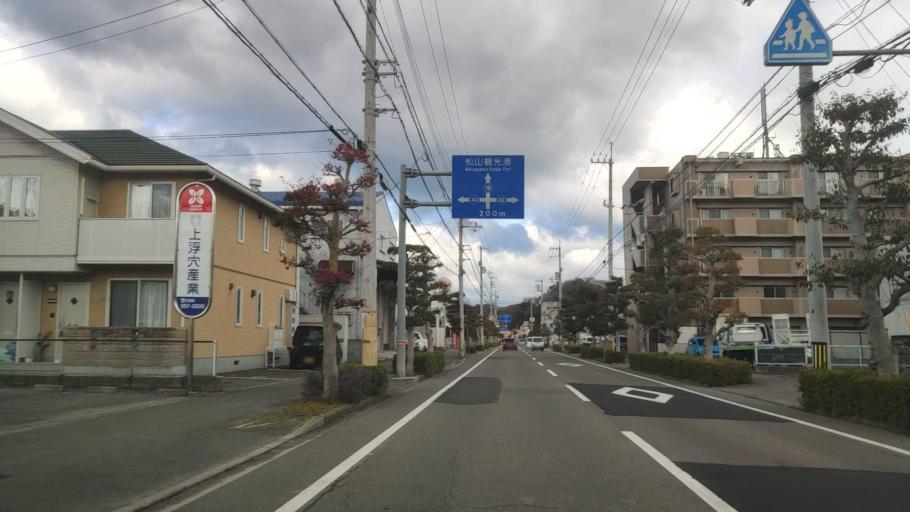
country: JP
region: Ehime
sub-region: Shikoku-chuo Shi
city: Matsuyama
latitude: 33.8647
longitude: 132.7258
